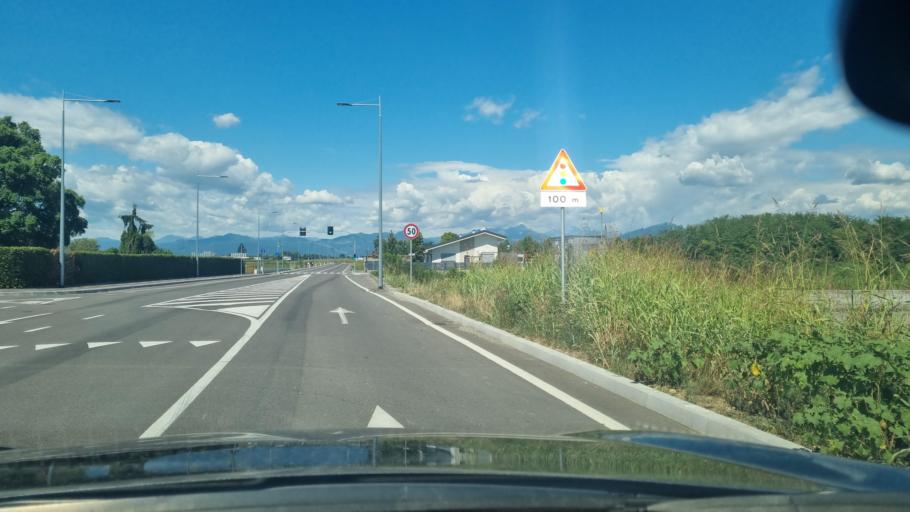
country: IT
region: Lombardy
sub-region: Provincia di Bergamo
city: Ghisalba
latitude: 45.5943
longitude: 9.7714
